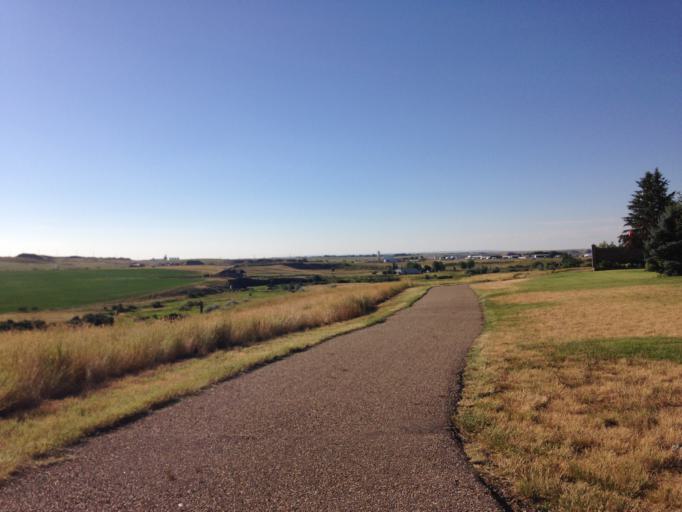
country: CA
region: Alberta
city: Medicine Hat
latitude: 49.9963
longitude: -110.6231
